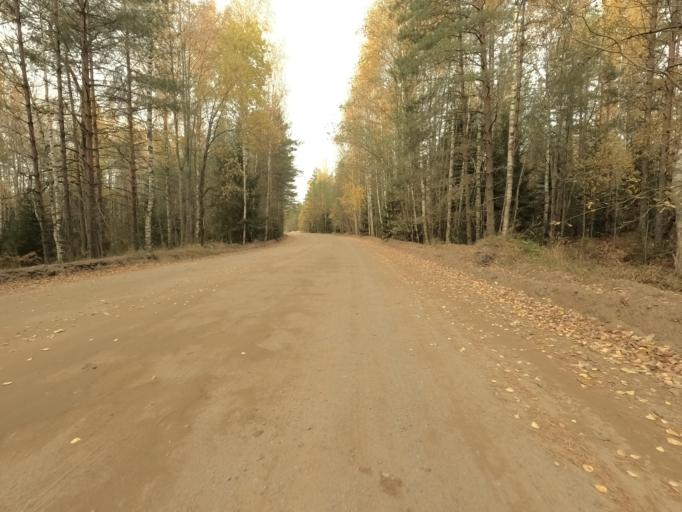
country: RU
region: Leningrad
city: Priladozhskiy
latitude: 59.6866
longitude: 31.3620
